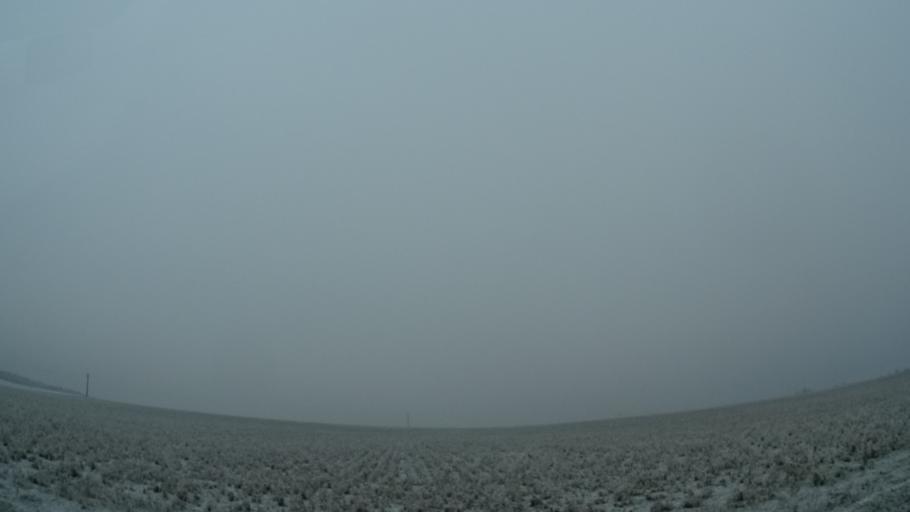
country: DE
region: Bavaria
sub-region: Regierungsbezirk Unterfranken
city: Volkach
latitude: 49.8349
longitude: 10.2629
